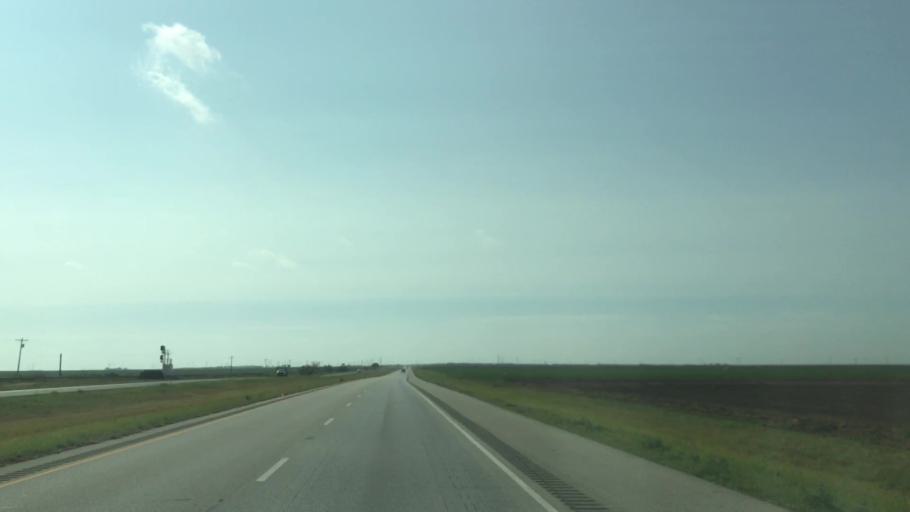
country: US
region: Texas
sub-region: Scurry County
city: Snyder
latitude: 32.6682
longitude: -100.7979
